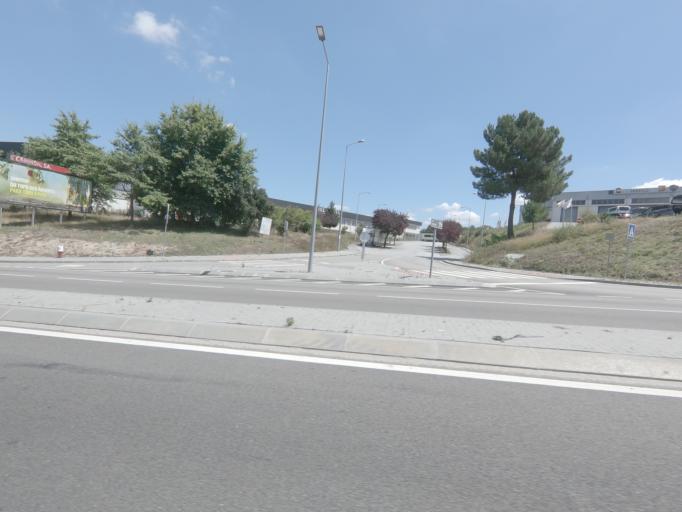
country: PT
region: Porto
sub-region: Paredes
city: Paredes
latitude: 41.1977
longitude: -8.3076
